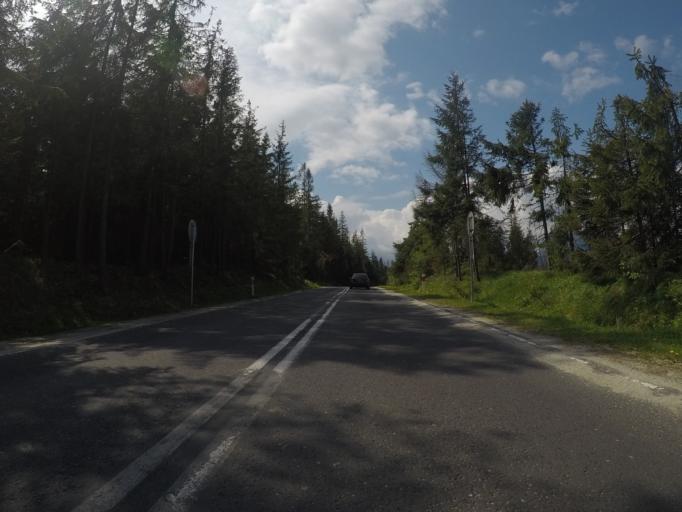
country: PL
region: Lesser Poland Voivodeship
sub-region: Powiat tatrzanski
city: Bukowina Tatrzanska
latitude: 49.2923
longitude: 20.1141
